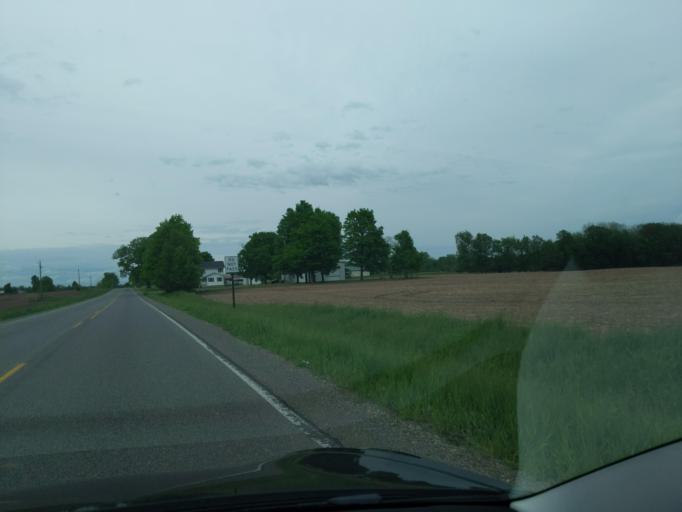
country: US
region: Michigan
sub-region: Ingham County
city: Leslie
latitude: 42.4819
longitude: -84.4236
